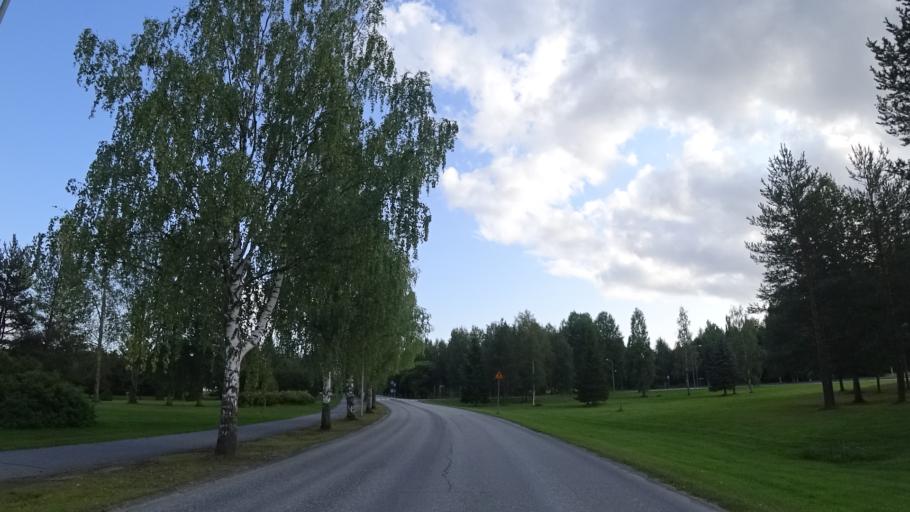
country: FI
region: North Karelia
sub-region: Pielisen Karjala
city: Lieksa
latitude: 63.3281
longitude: 30.0226
